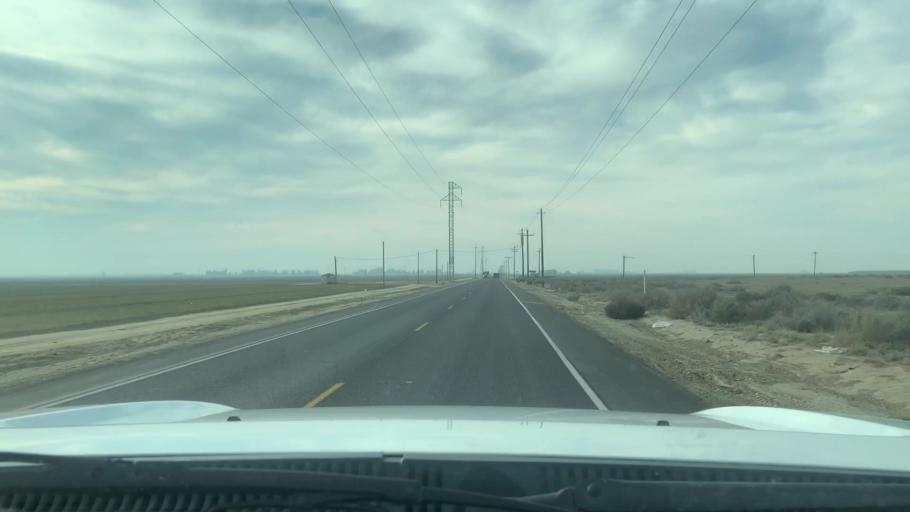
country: US
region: California
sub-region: Kern County
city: Shafter
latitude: 35.4421
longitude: -119.3651
